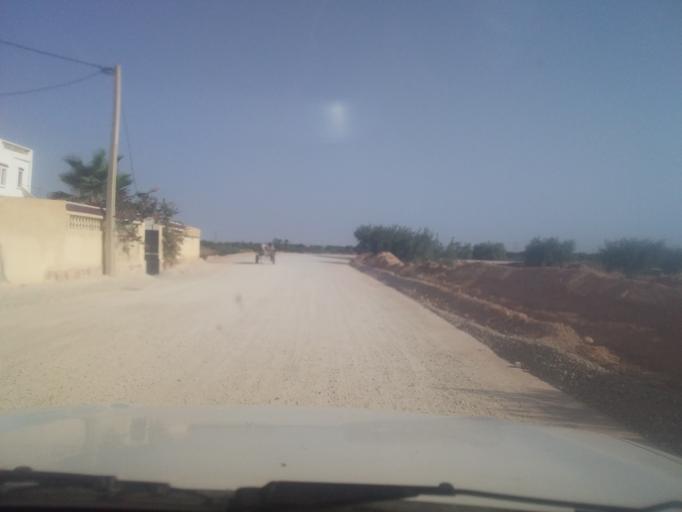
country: TN
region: Qabis
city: Matmata
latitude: 33.5939
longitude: 10.2717
